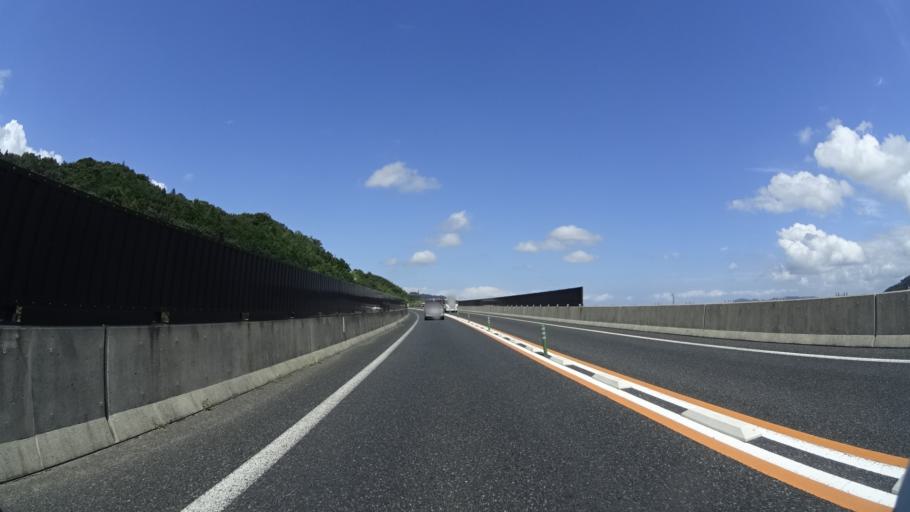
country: JP
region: Tottori
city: Tottori
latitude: 35.4384
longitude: 134.2036
